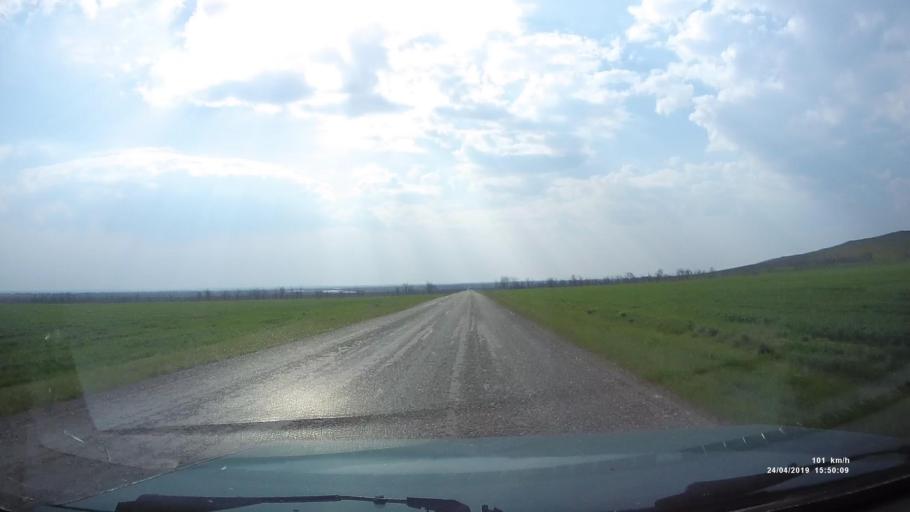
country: RU
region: Kalmykiya
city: Yashalta
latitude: 46.6040
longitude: 42.6385
